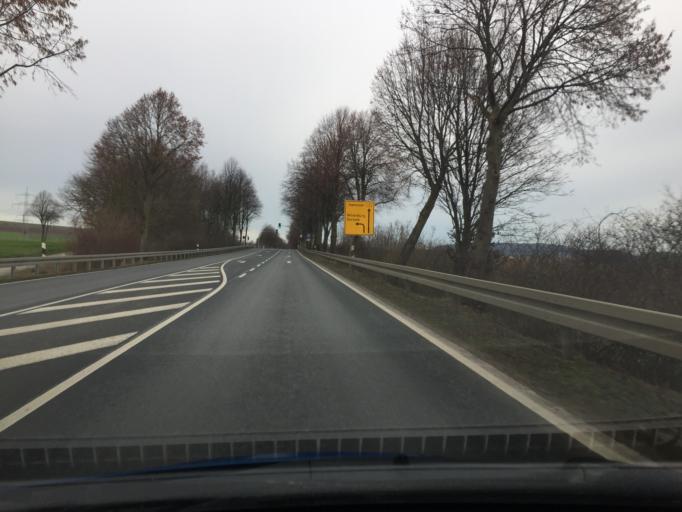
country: DE
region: Lower Saxony
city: Elze
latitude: 52.1370
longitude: 9.7316
